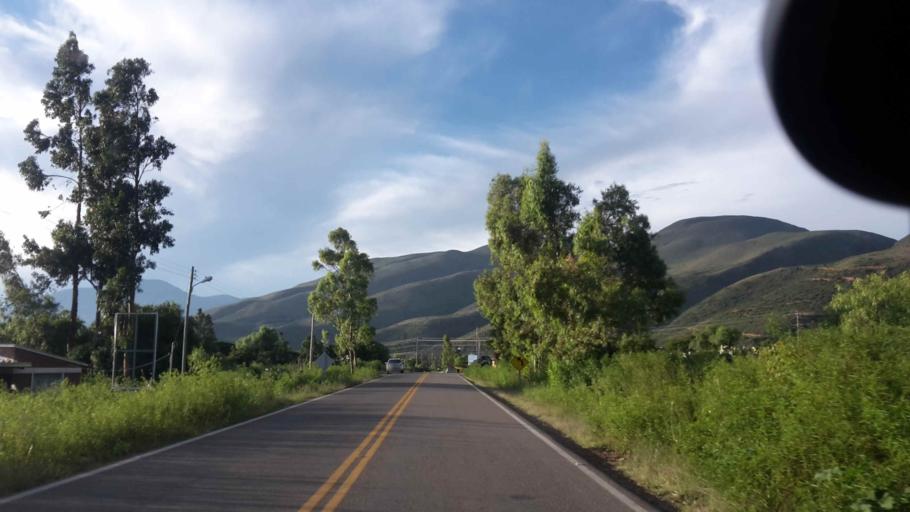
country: BO
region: Cochabamba
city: Arani
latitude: -17.5772
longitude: -65.7582
